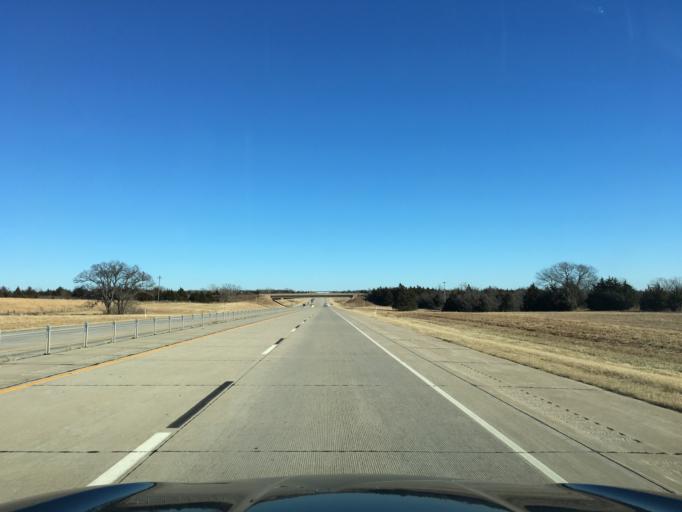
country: US
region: Oklahoma
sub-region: Payne County
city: Yale
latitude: 36.2250
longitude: -96.6819
